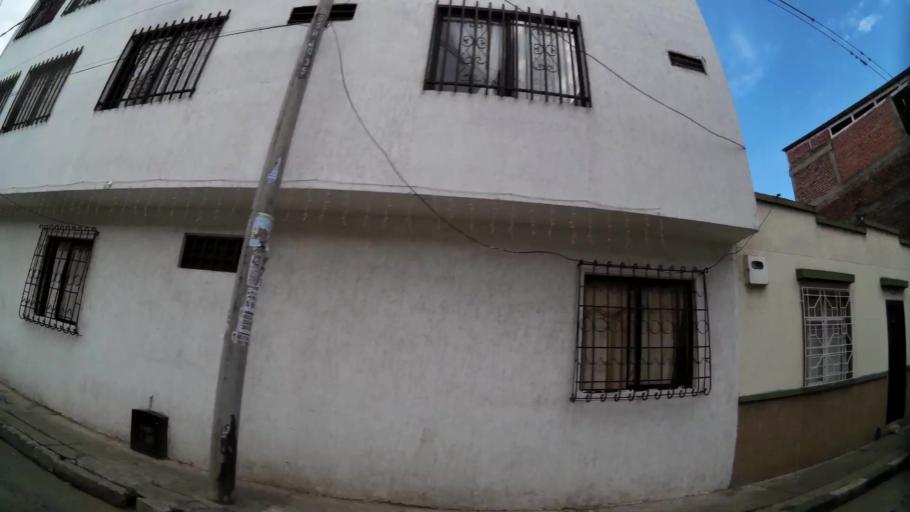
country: CO
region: Valle del Cauca
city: Cali
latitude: 3.4244
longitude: -76.5234
